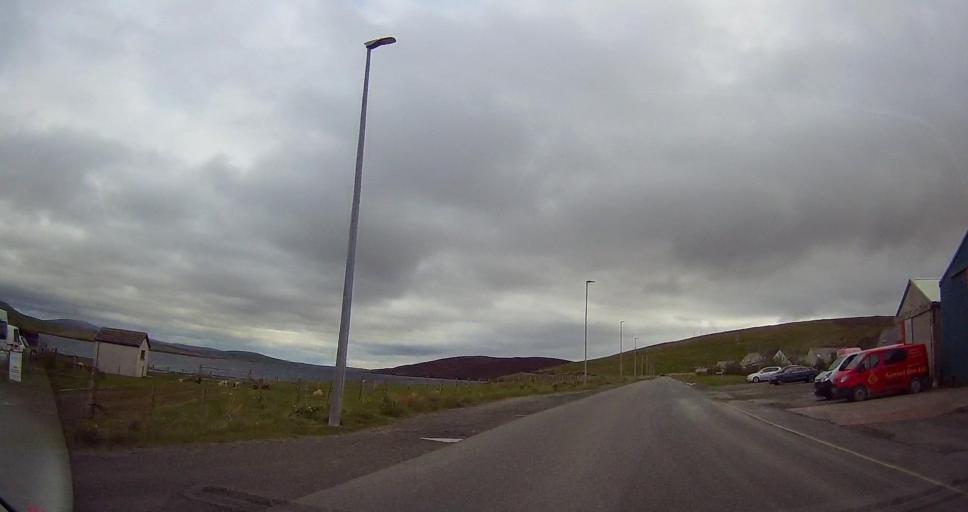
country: GB
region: Scotland
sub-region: Shetland Islands
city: Lerwick
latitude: 60.3980
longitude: -1.3543
